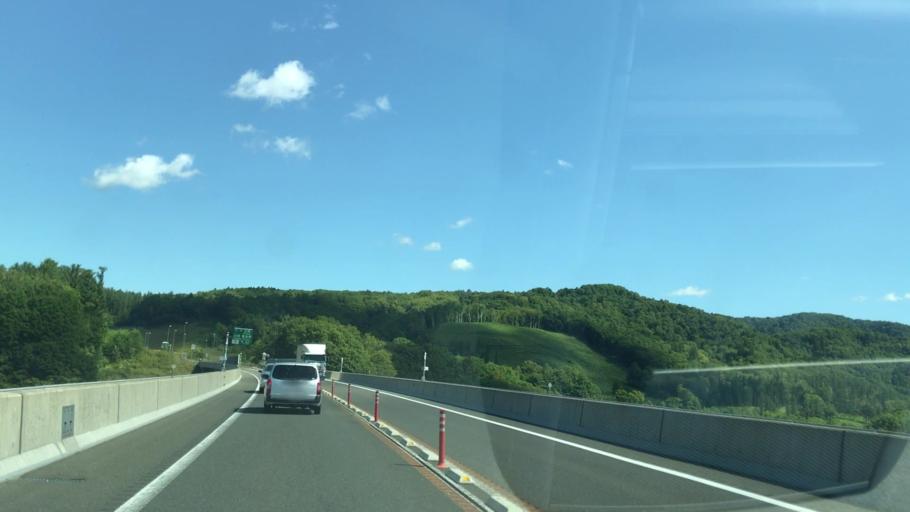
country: JP
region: Hokkaido
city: Shimo-furano
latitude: 42.9761
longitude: 142.4050
